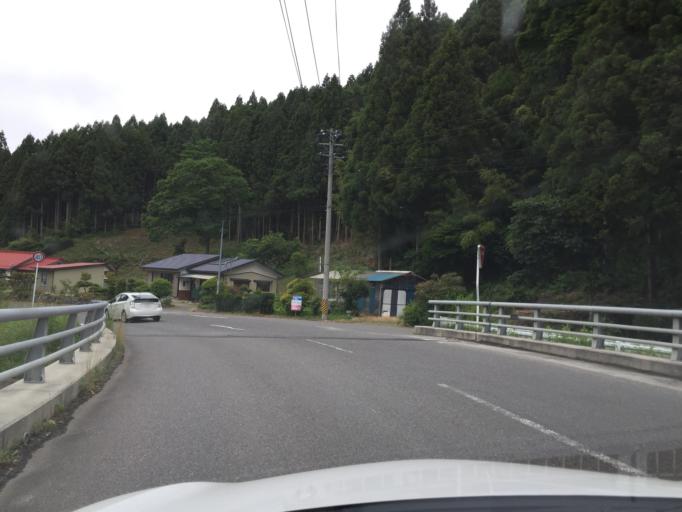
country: JP
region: Fukushima
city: Funehikimachi-funehiki
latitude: 37.3291
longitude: 140.6959
